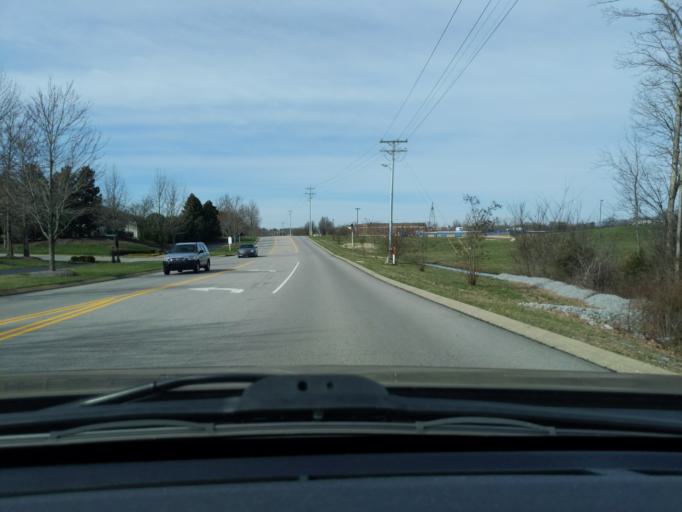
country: US
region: Tennessee
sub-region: Wilson County
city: Rural Hill
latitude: 36.1667
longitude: -86.4767
